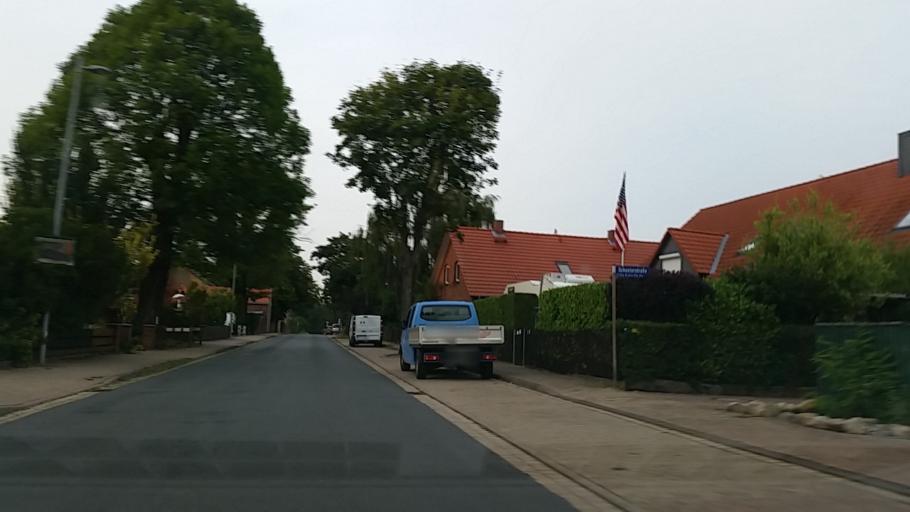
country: DE
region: Lower Saxony
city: Klein Schwulper
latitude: 52.3373
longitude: 10.4485
